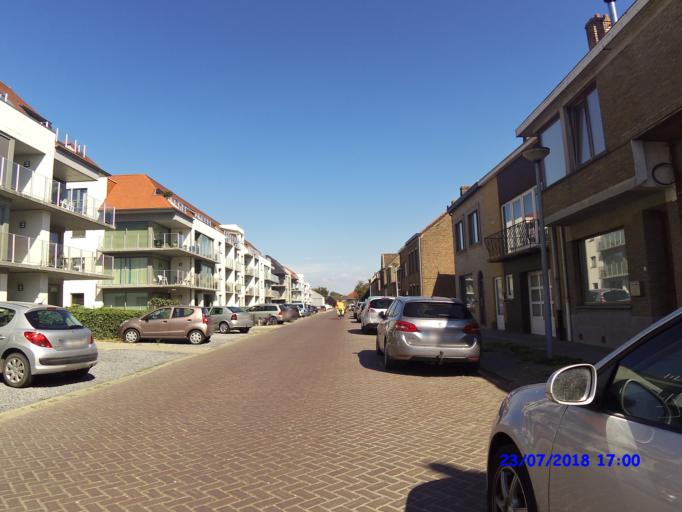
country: BE
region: Flanders
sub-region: Provincie West-Vlaanderen
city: Veurne
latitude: 51.0727
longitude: 2.6735
